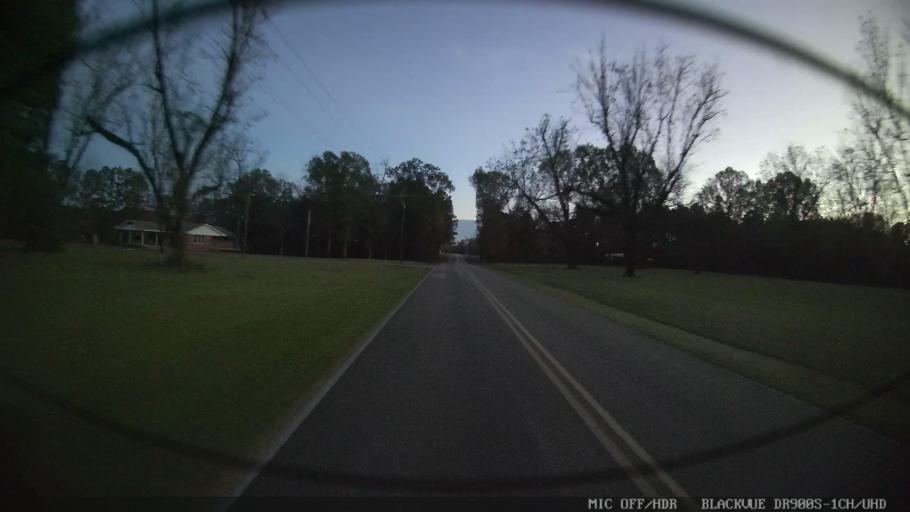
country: US
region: Mississippi
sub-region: Forrest County
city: Hattiesburg
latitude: 31.1738
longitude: -89.2186
